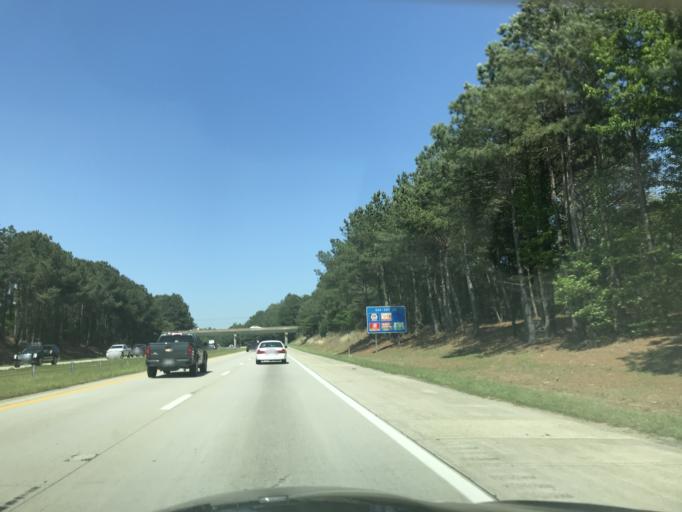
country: US
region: North Carolina
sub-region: Johnston County
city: Clayton
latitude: 35.5962
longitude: -78.5662
